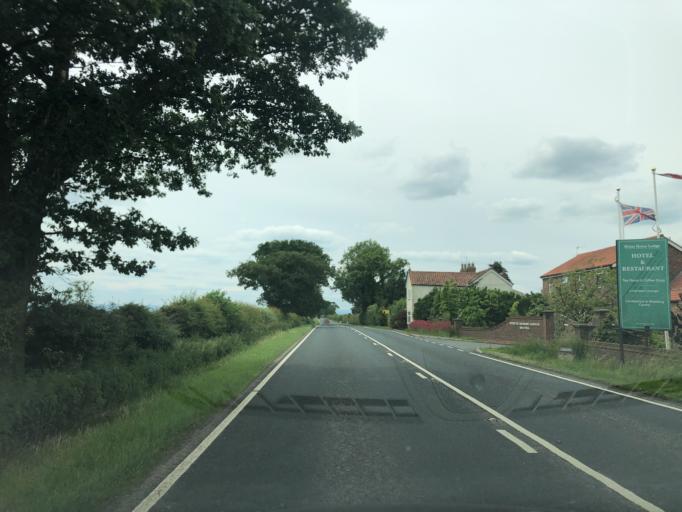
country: GB
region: England
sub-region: North Yorkshire
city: Thirsk
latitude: 54.2317
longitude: -1.2974
